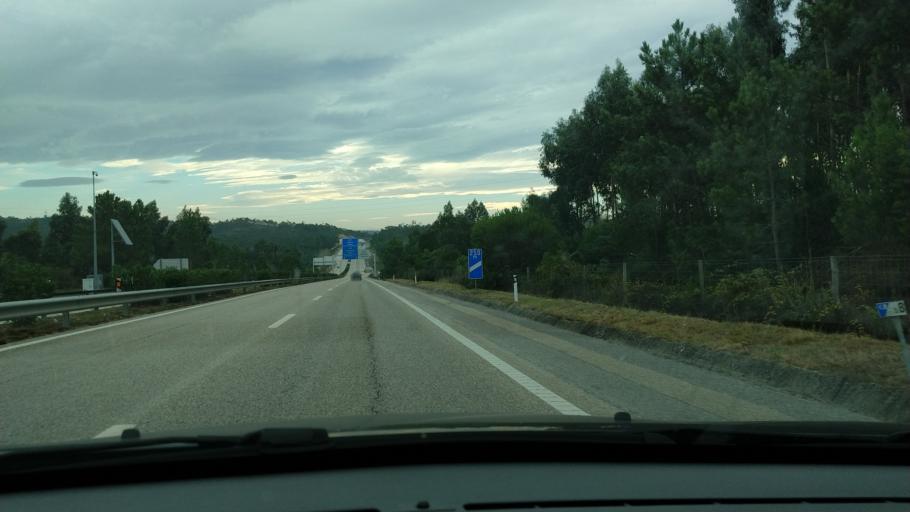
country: PT
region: Coimbra
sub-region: Figueira da Foz
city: Alhadas
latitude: 40.1536
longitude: -8.7983
